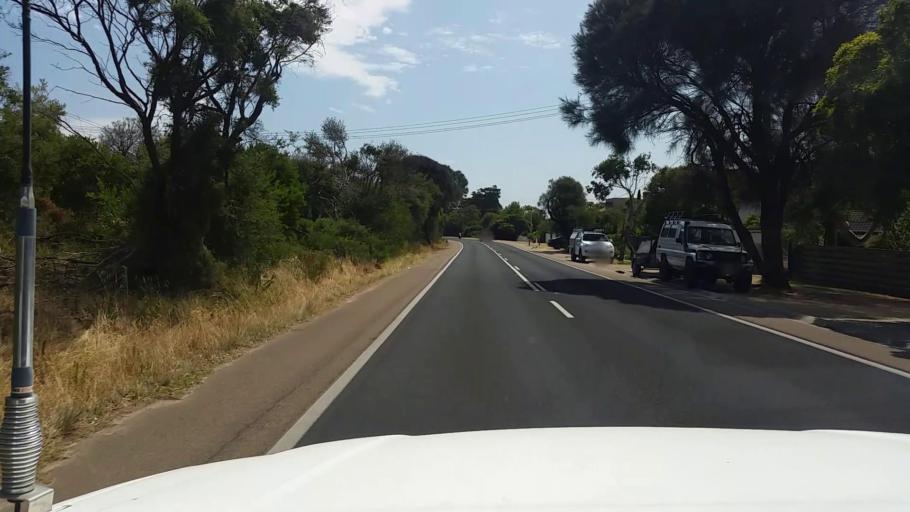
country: AU
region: Victoria
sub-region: Mornington Peninsula
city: Mornington
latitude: -38.2399
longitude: 145.0297
